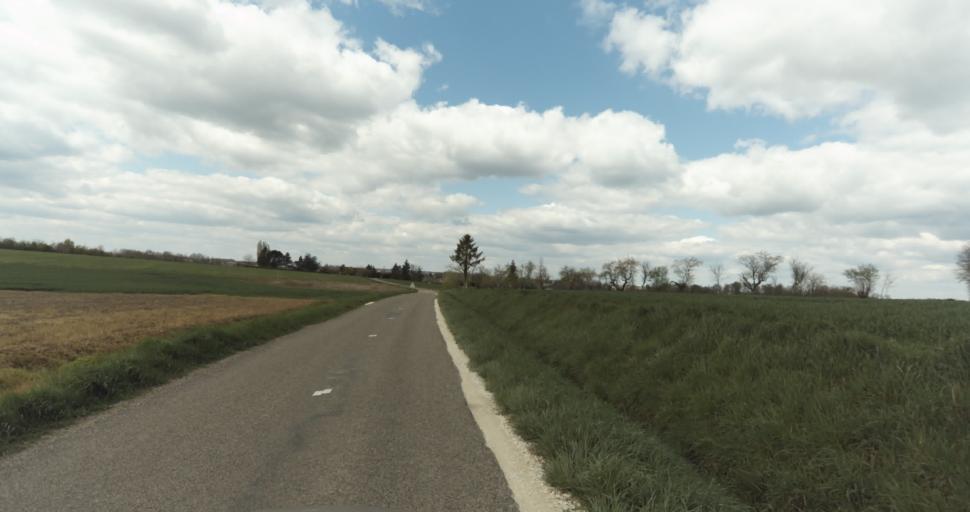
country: FR
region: Bourgogne
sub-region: Departement de la Cote-d'Or
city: Auxonne
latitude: 47.1834
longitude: 5.4111
